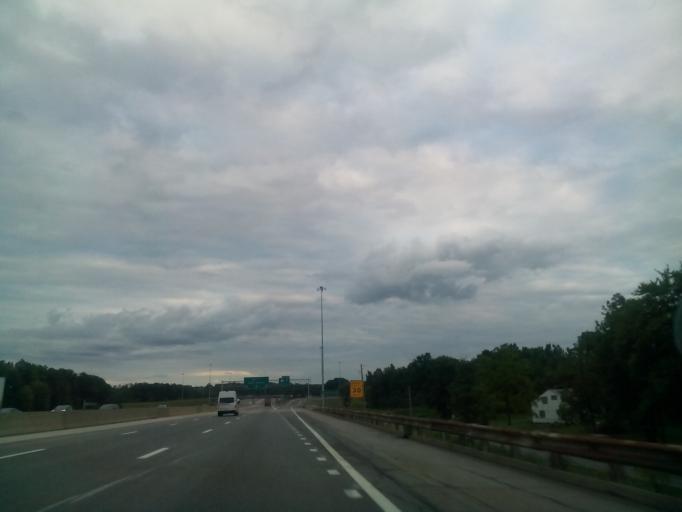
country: US
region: Ohio
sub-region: Trumbull County
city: Newton Falls
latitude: 41.2214
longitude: -80.9589
